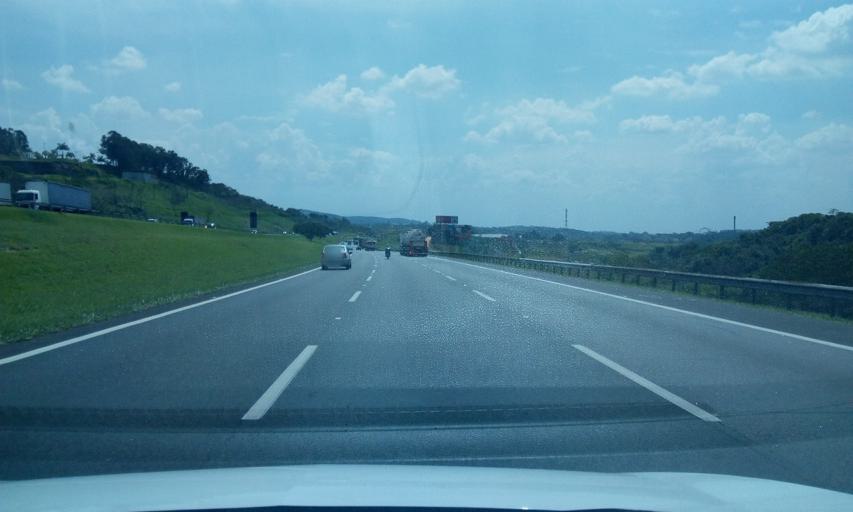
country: BR
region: Sao Paulo
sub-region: Louveira
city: Louveira
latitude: -23.1145
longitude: -46.9975
